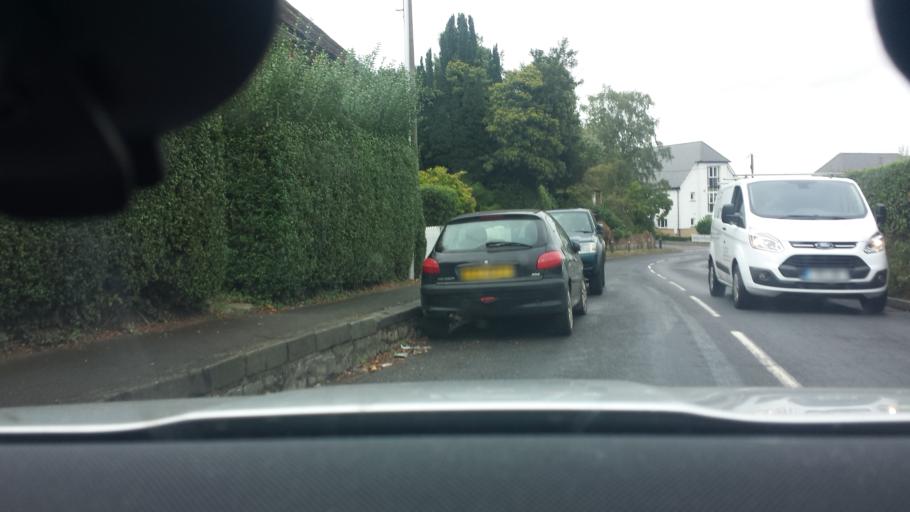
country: GB
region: England
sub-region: Kent
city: Harrietsham
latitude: 51.2461
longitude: 0.6066
